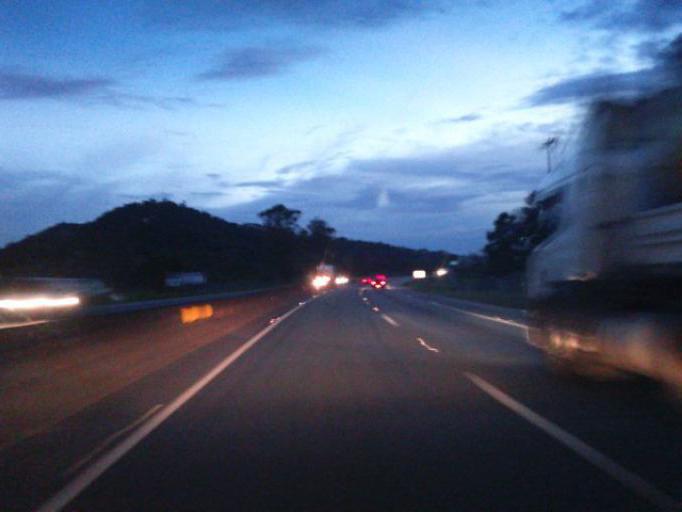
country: BR
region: Santa Catarina
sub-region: Barra Velha
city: Barra Velha
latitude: -26.5662
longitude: -48.7197
